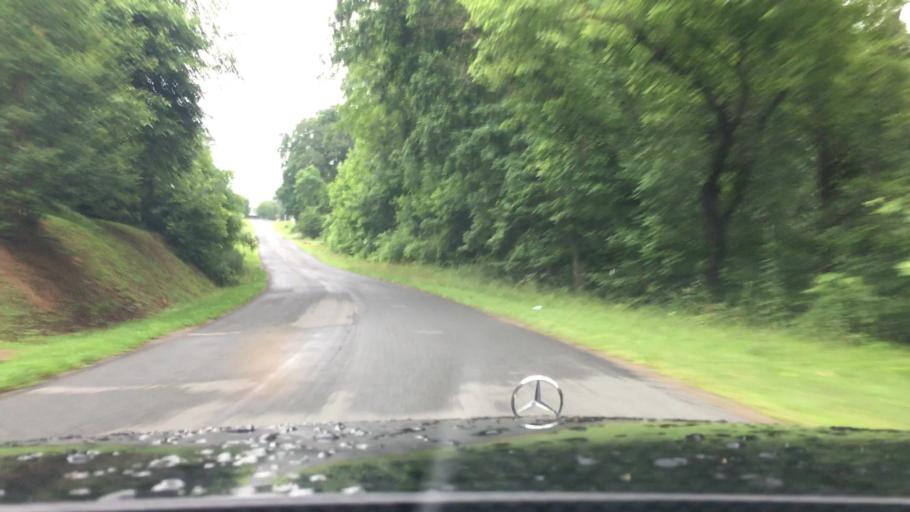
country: US
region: Virginia
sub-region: Pittsylvania County
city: Hurt
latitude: 37.0965
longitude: -79.2984
